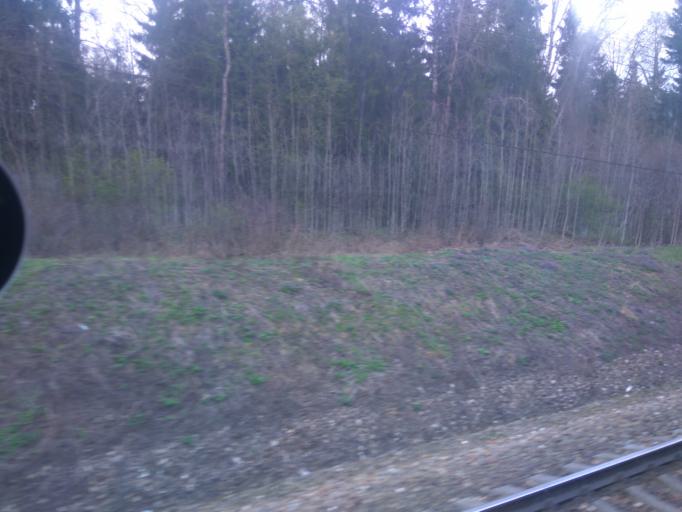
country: RU
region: Moskovskaya
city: Svatkovo
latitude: 56.3834
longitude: 38.2622
